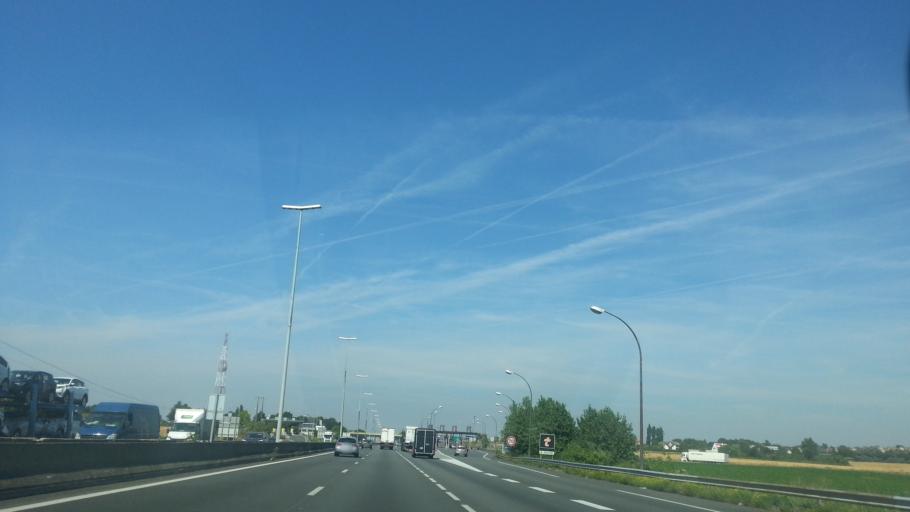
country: FR
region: Ile-de-France
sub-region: Departement du Val-d'Oise
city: Survilliers
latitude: 49.0817
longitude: 2.5515
